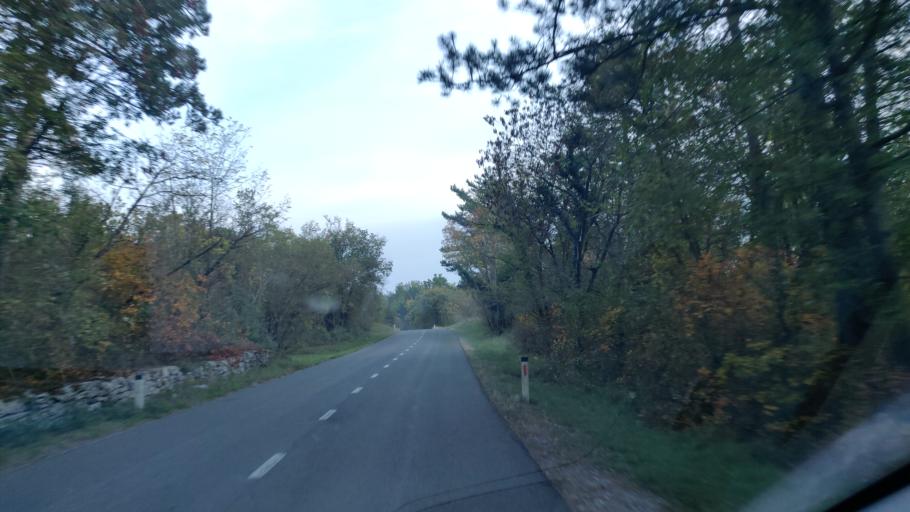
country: SI
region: Sezana
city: Sezana
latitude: 45.7981
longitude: 13.8541
